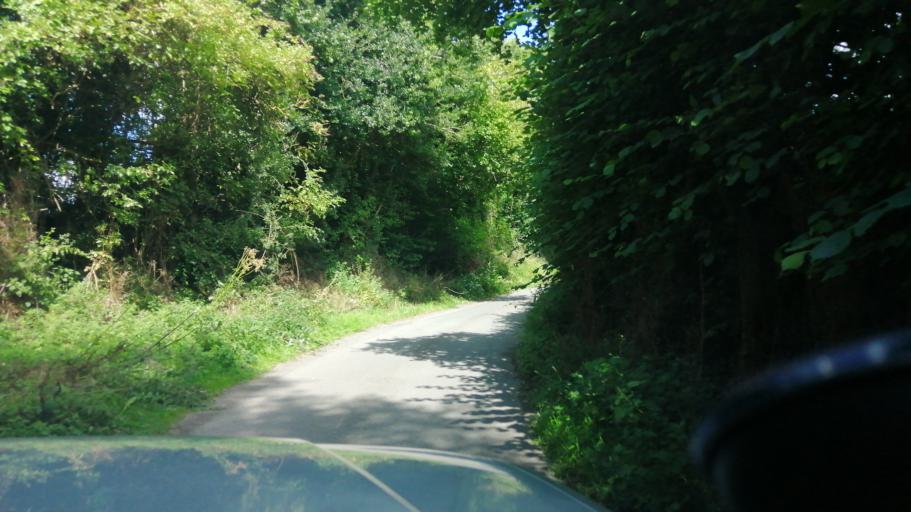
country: GB
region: England
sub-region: Herefordshire
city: Thruxton
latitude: 52.0114
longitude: -2.8126
